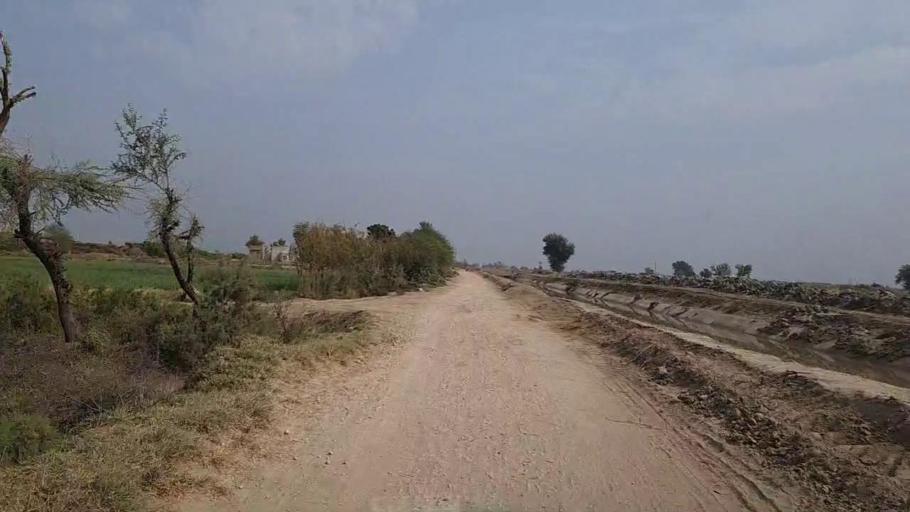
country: PK
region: Sindh
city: Mirwah Gorchani
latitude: 25.3995
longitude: 69.0825
